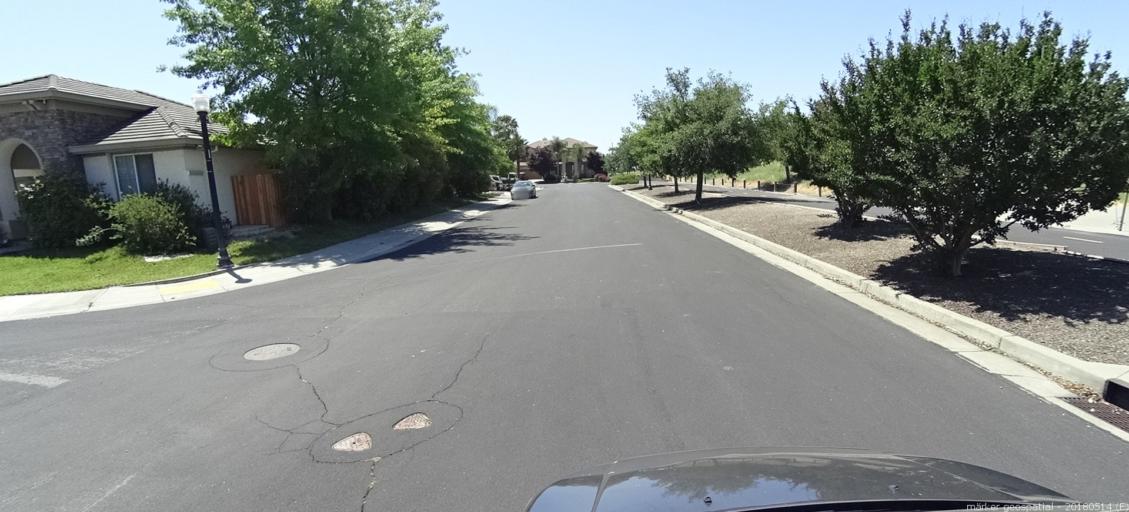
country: US
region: California
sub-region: Yolo County
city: West Sacramento
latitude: 38.6292
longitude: -121.5328
